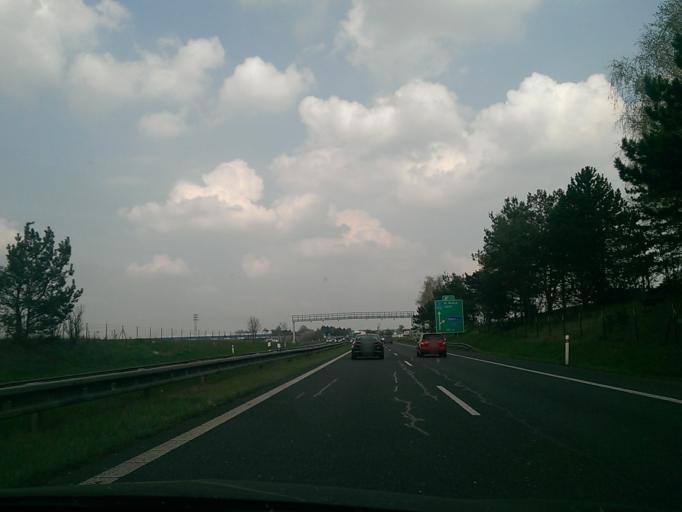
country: CZ
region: Central Bohemia
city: Benatky nad Jizerou
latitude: 50.2745
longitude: 14.8188
